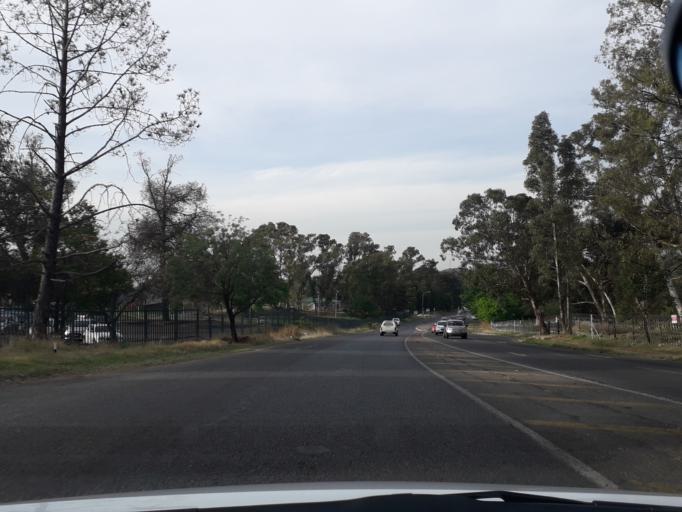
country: ZA
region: Gauteng
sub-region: City of Johannesburg Metropolitan Municipality
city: Modderfontein
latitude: -26.1342
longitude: 28.1181
